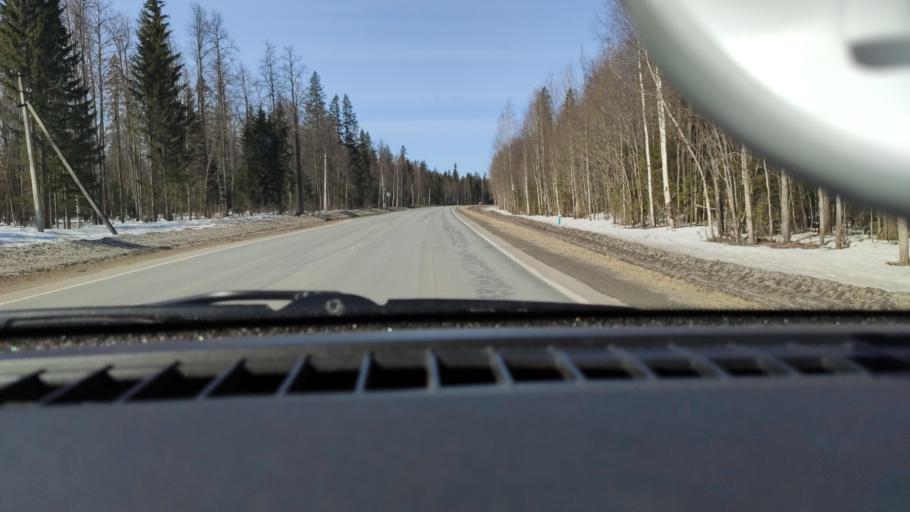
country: RU
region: Perm
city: Perm
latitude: 58.2138
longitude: 56.1787
